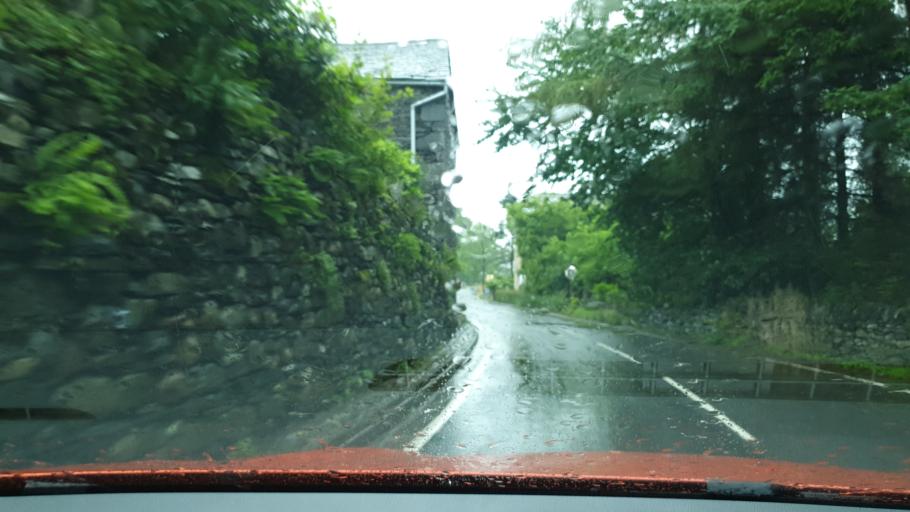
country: GB
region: England
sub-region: Cumbria
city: Ambleside
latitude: 54.3619
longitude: -3.0786
